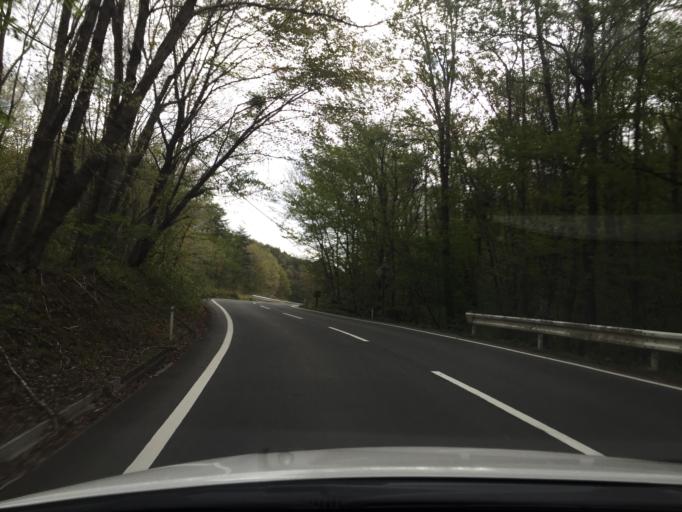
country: JP
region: Fukushima
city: Yanagawamachi-saiwaicho
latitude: 37.7221
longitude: 140.7297
